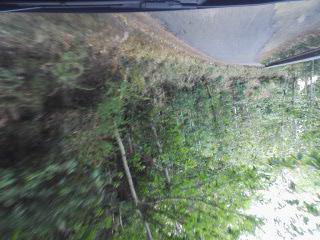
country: IT
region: Calabria
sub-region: Provincia di Vibo-Valentia
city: Nardodipace
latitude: 38.4420
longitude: 16.3393
